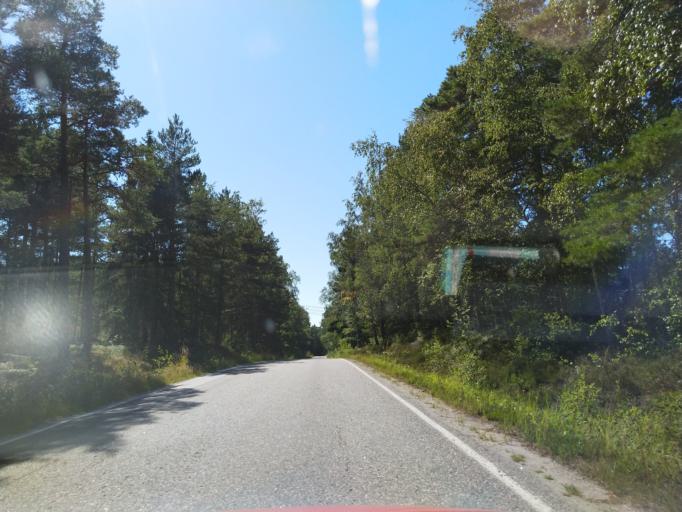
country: FI
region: Varsinais-Suomi
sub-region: Aboland-Turunmaa
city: Dragsfjaerd
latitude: 60.0163
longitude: 22.4764
